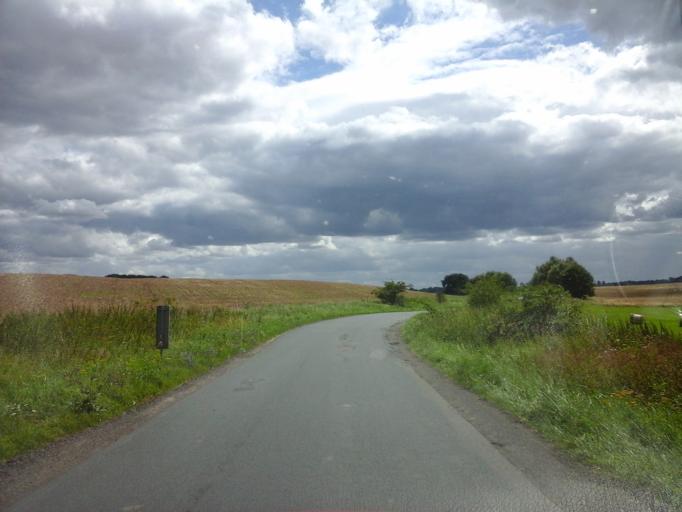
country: PL
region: West Pomeranian Voivodeship
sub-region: Powiat policki
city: Przeclaw
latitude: 53.4114
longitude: 14.4236
